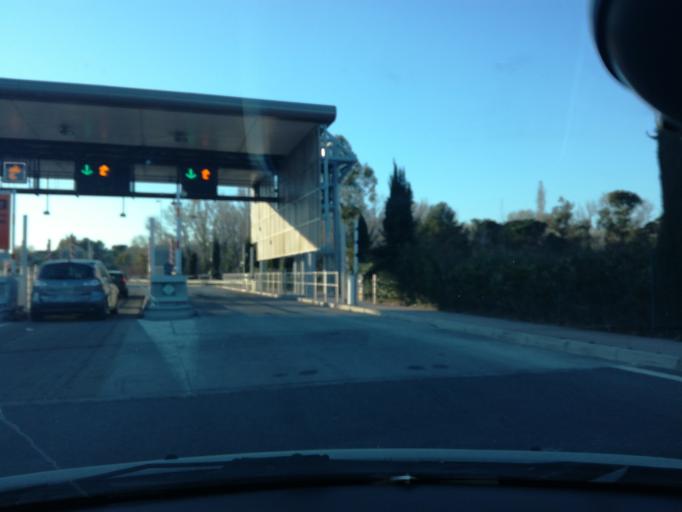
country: FR
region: Provence-Alpes-Cote d'Azur
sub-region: Departement du Var
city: Frejus
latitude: 43.4721
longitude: 6.7438
